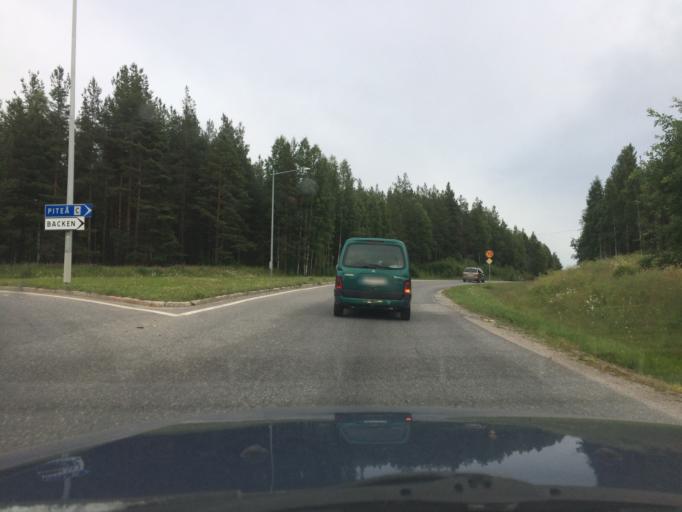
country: SE
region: Norrbotten
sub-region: Pitea Kommun
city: Bergsviken
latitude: 65.3301
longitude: 21.4251
